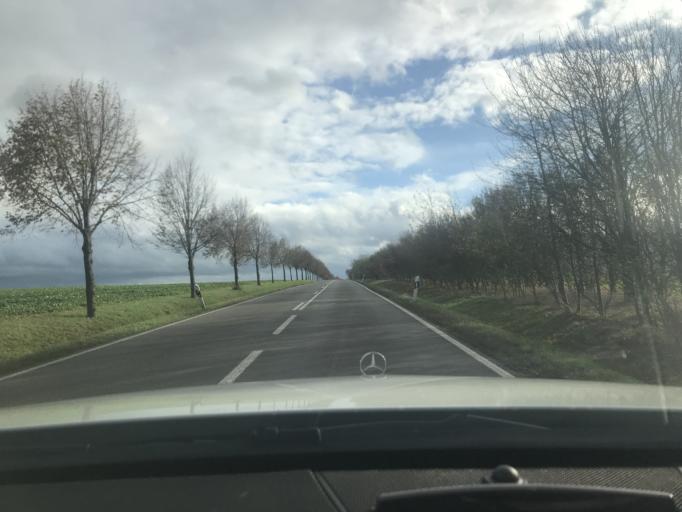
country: DE
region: Thuringia
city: Bufleben
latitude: 50.9875
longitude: 10.7420
